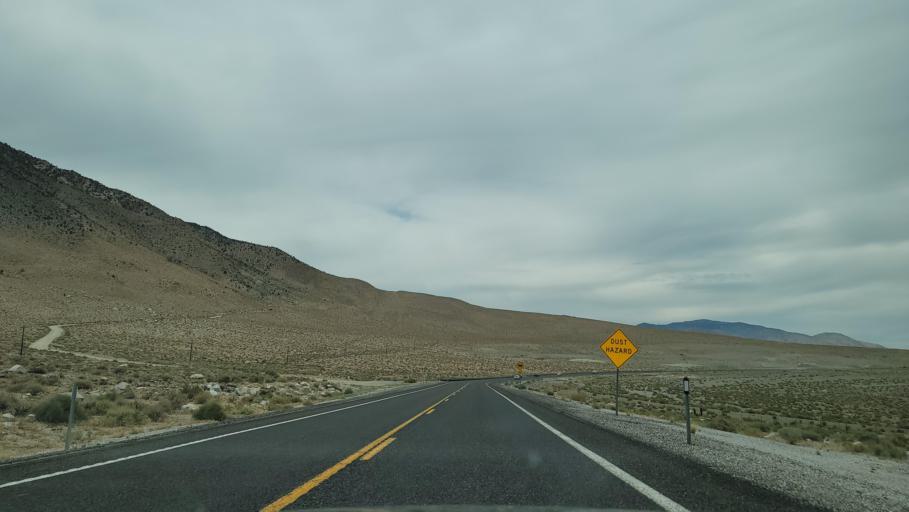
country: US
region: Nevada
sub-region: Mineral County
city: Hawthorne
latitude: 38.5817
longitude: -118.7053
